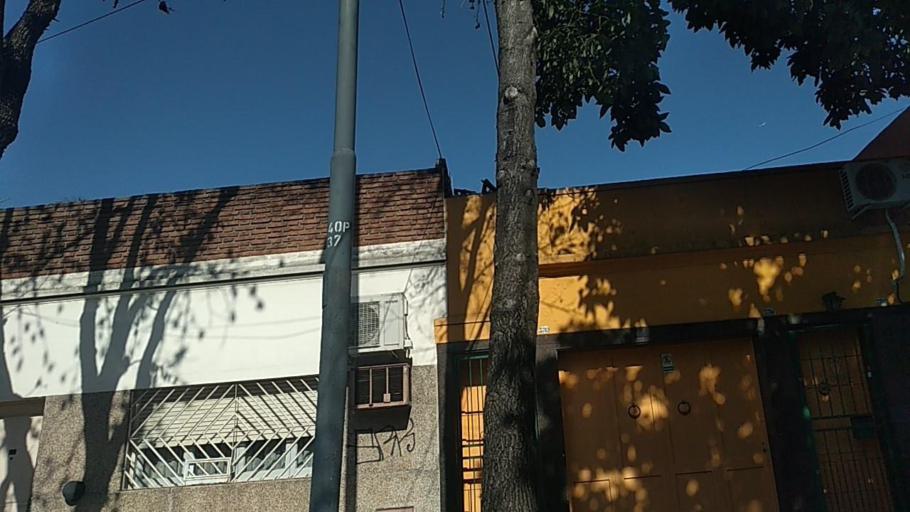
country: AR
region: Buenos Aires F.D.
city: Villa Santa Rita
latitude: -34.6105
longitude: -58.4969
